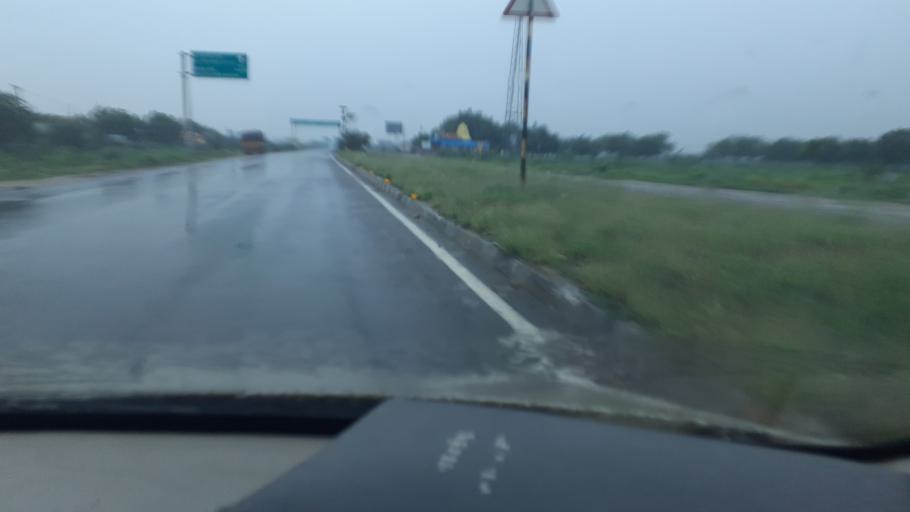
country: IN
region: Tamil Nadu
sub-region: Virudhunagar
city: Sattur
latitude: 9.3948
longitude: 77.9157
